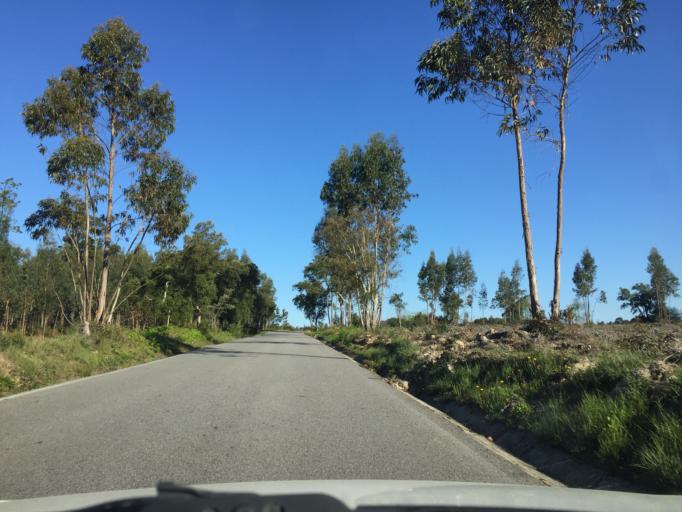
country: PT
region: Aveiro
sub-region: Anadia
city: Sangalhos
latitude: 40.4571
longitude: -8.4910
